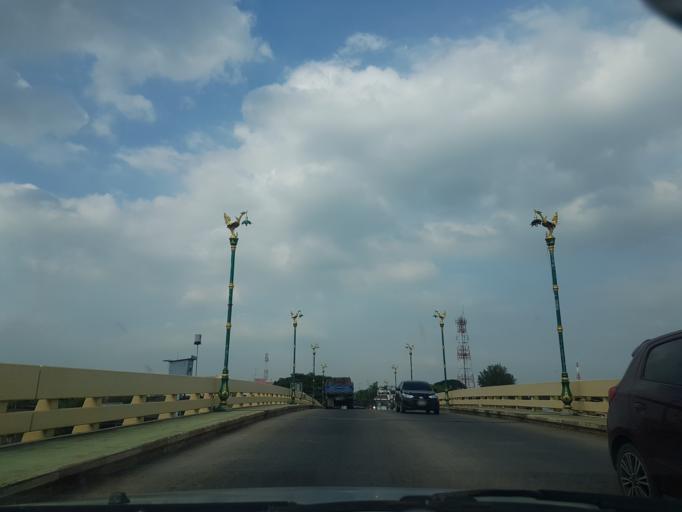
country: TH
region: Phra Nakhon Si Ayutthaya
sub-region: Amphoe Tha Ruea
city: Tha Ruea
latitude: 14.5598
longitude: 100.7198
